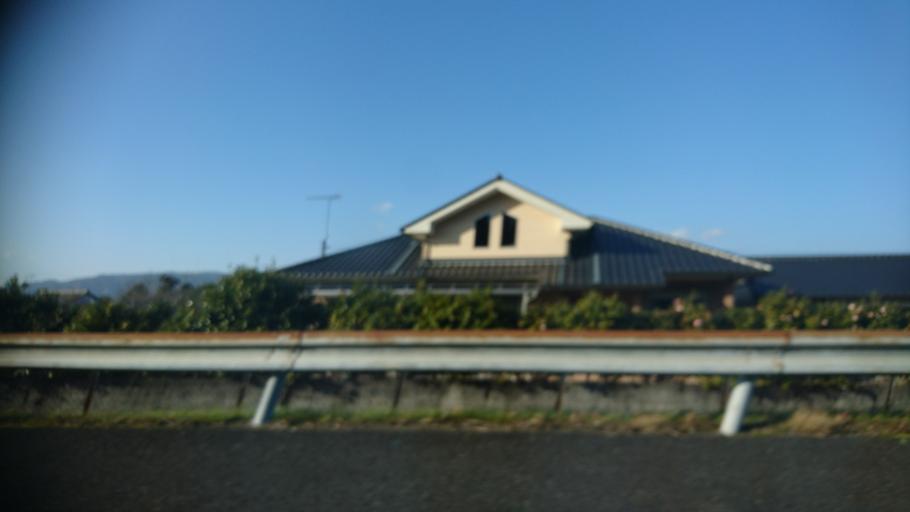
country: JP
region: Miyazaki
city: Kobayashi
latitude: 32.0288
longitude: 130.8647
